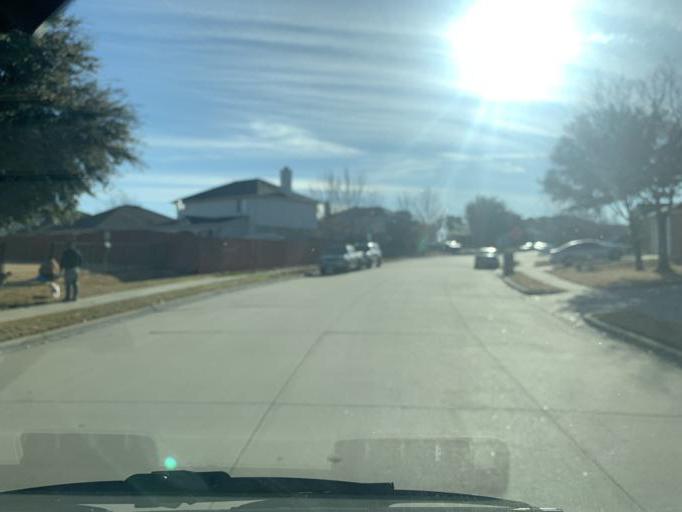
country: US
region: Texas
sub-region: Dallas County
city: Duncanville
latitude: 32.6556
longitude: -96.9734
